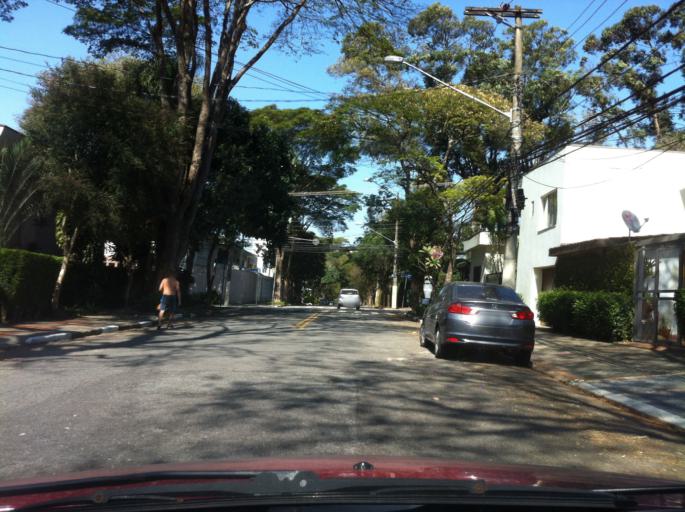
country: BR
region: Sao Paulo
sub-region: Diadema
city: Diadema
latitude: -23.6226
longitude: -46.6453
